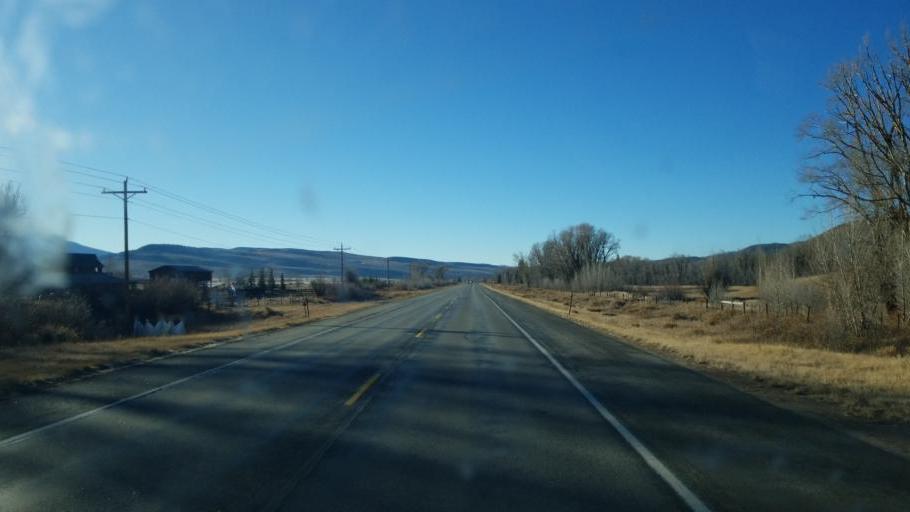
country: US
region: Colorado
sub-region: Gunnison County
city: Crested Butte
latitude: 38.7659
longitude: -106.8649
